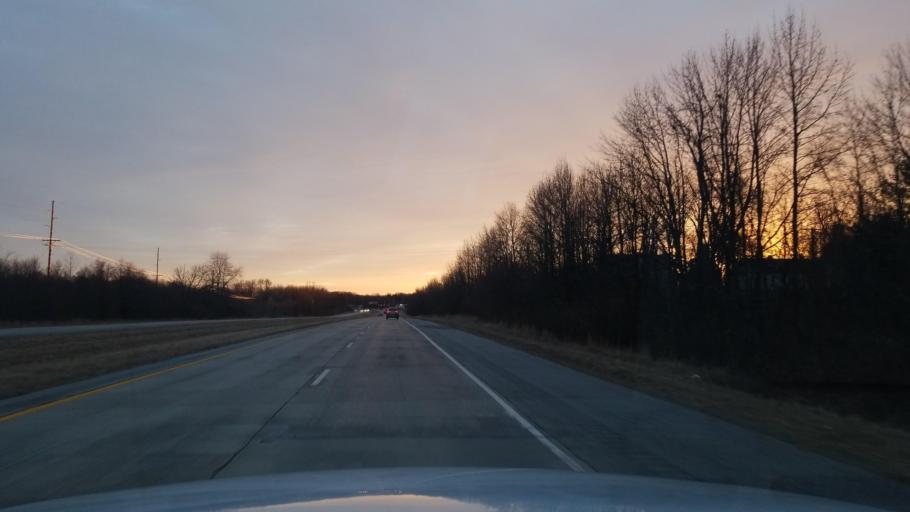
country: US
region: Indiana
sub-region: Posey County
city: Mount Vernon
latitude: 37.9423
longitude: -87.7290
